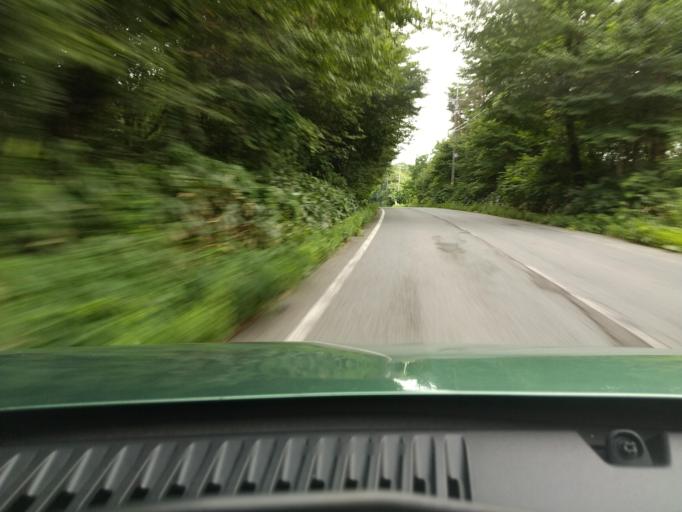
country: JP
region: Akita
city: Akita
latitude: 39.7612
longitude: 140.1331
